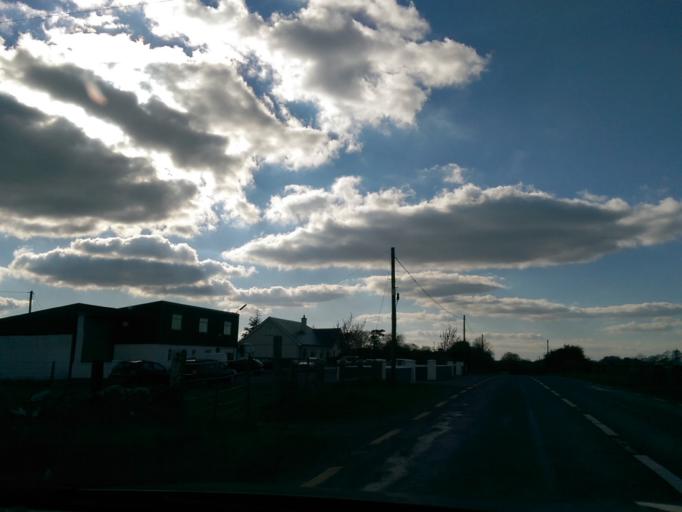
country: IE
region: Connaught
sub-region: County Galway
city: Portumna
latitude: 53.1903
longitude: -8.3780
